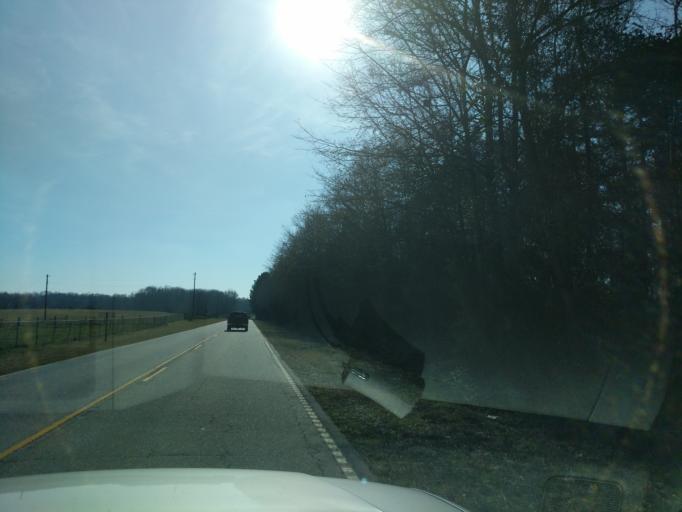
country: US
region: South Carolina
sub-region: Laurens County
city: Watts Mills
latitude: 34.6320
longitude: -81.9761
